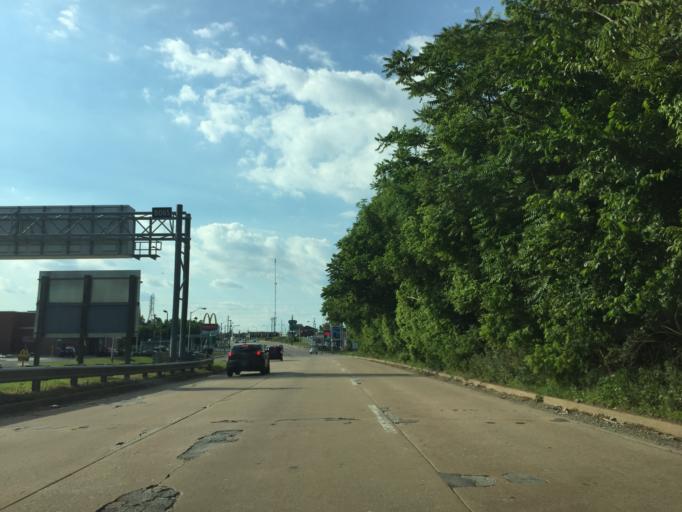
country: US
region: Maryland
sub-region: Baltimore County
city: Rosedale
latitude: 39.3144
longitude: -76.5439
